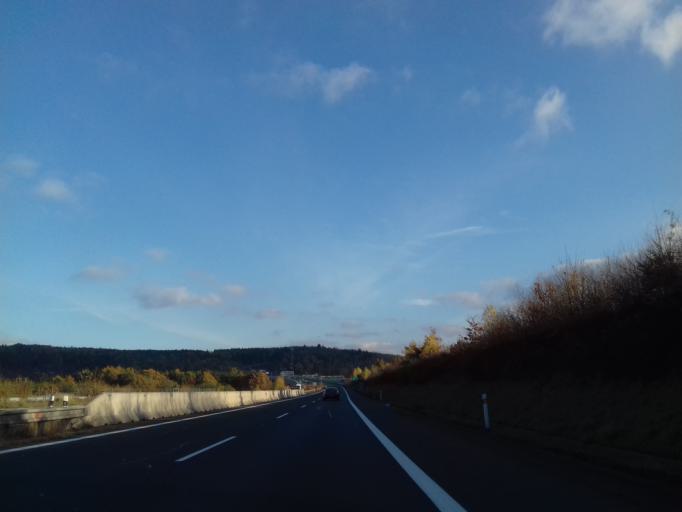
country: CZ
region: Plzensky
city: Stenovice
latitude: 49.6836
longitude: 13.3899
